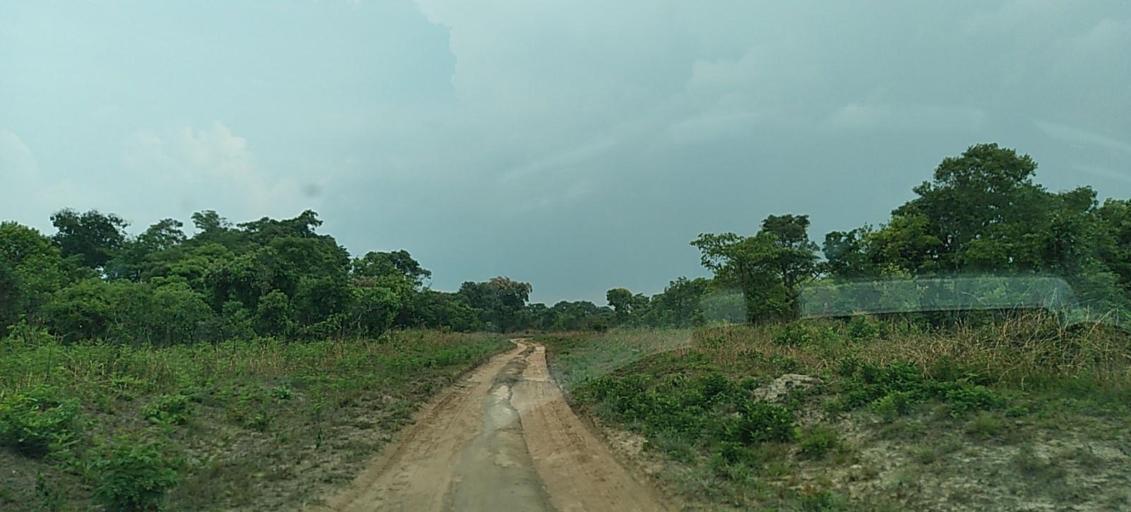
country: ZM
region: North-Western
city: Mwinilunga
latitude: -11.4342
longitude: 24.5942
